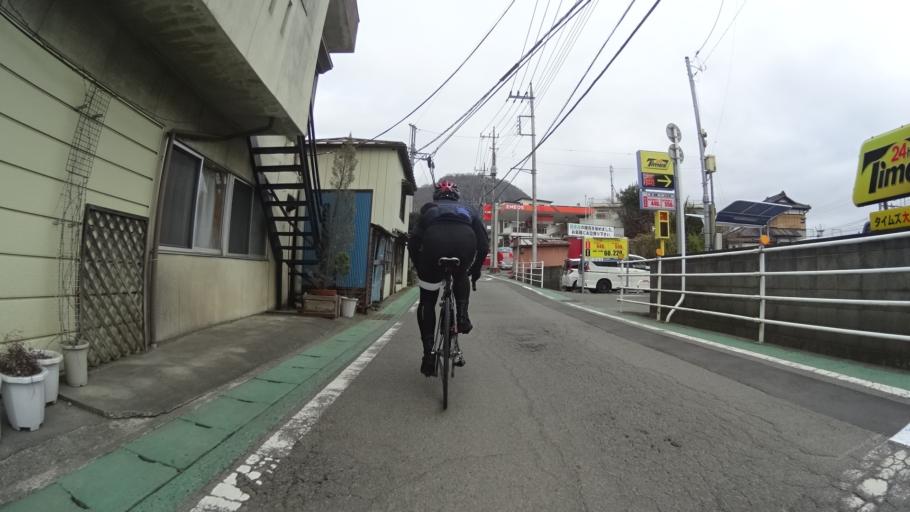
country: JP
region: Yamanashi
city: Otsuki
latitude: 35.6130
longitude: 138.9405
